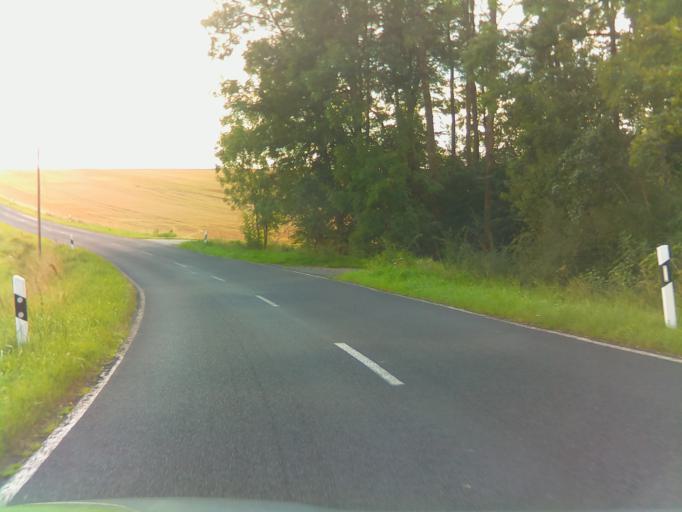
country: DE
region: Bavaria
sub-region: Regierungsbezirk Unterfranken
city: Rentweinsdorf
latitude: 50.0847
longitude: 10.8259
